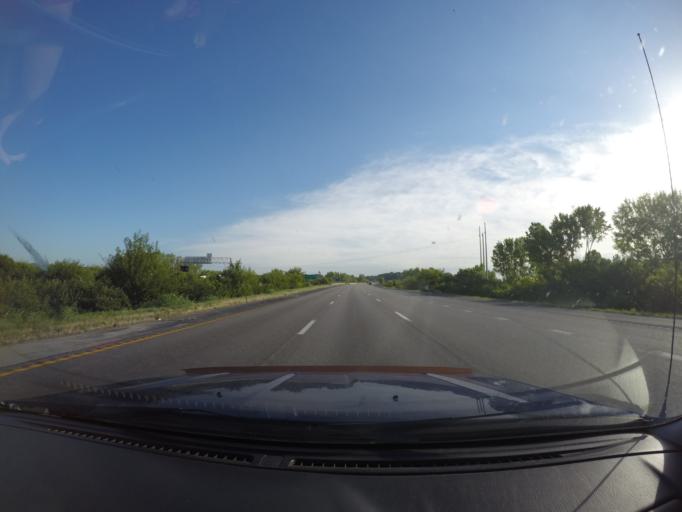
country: US
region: Missouri
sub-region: Platte County
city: Riverside
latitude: 39.1659
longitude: -94.6256
